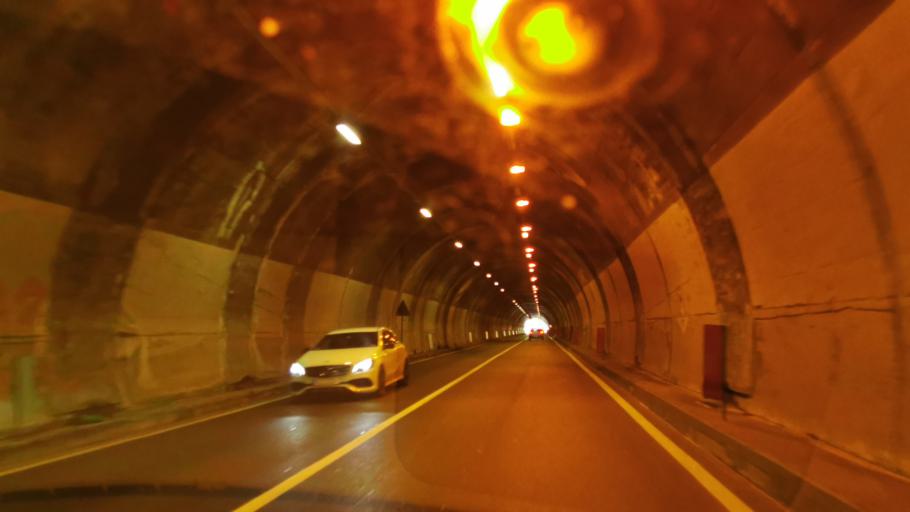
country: IT
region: Lombardy
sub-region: Provincia di Como
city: San Siro
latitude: 46.0706
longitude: 9.2751
